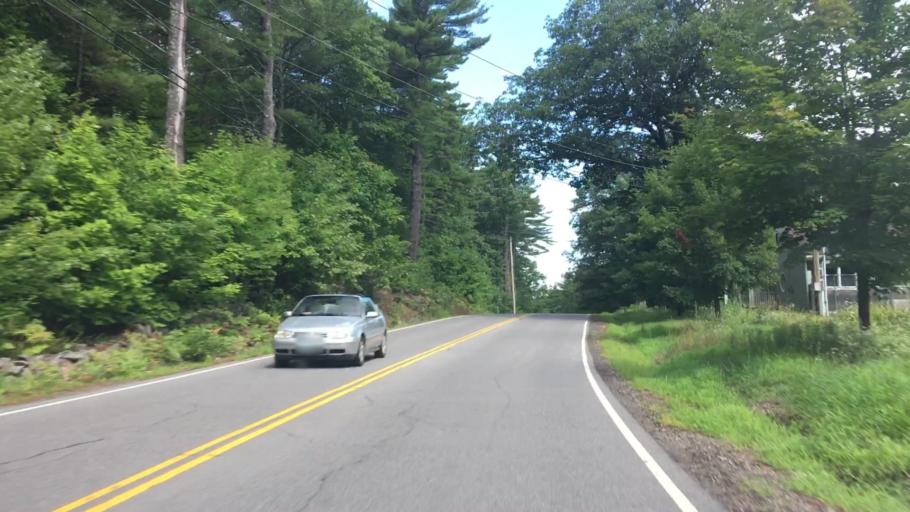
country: US
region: New Hampshire
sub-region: Belknap County
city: Meredith
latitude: 43.5970
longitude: -71.5179
